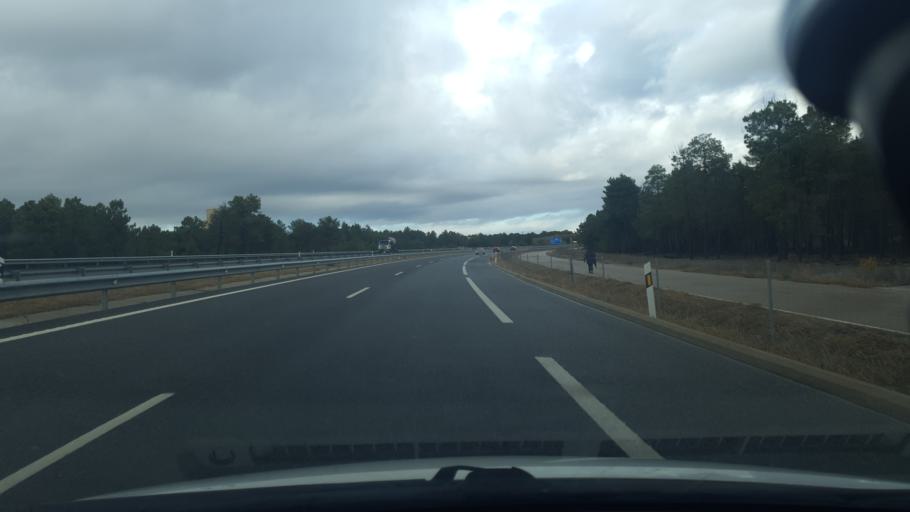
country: ES
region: Castille and Leon
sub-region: Provincia de Segovia
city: Sanchonuno
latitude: 41.3290
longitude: -4.3130
